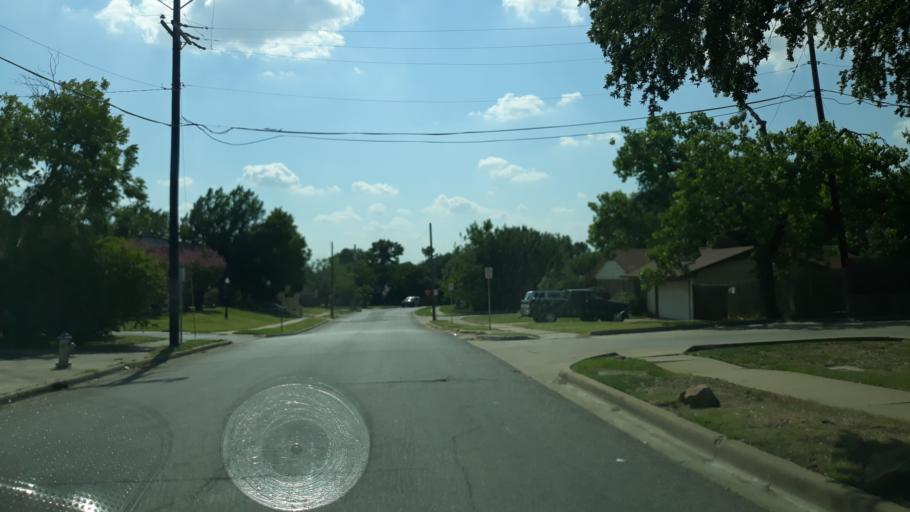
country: US
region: Texas
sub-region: Dallas County
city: Irving
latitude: 32.8499
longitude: -96.9935
